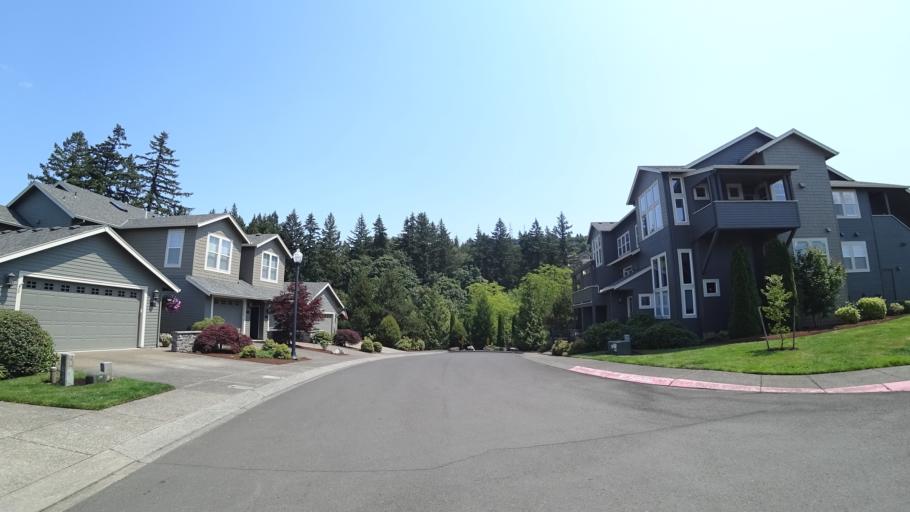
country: US
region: Oregon
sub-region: Multnomah County
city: Lents
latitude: 45.4598
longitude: -122.5565
